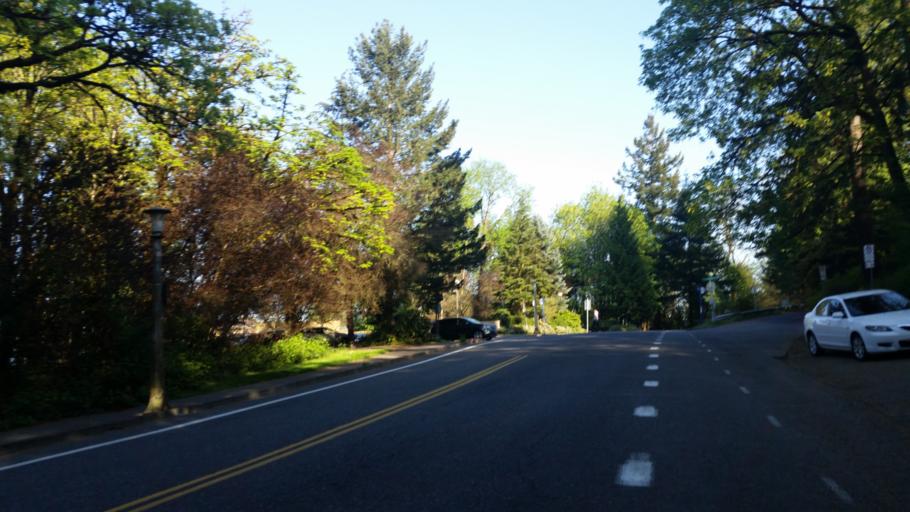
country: US
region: Oregon
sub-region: Multnomah County
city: Portland
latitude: 45.4834
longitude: -122.6841
